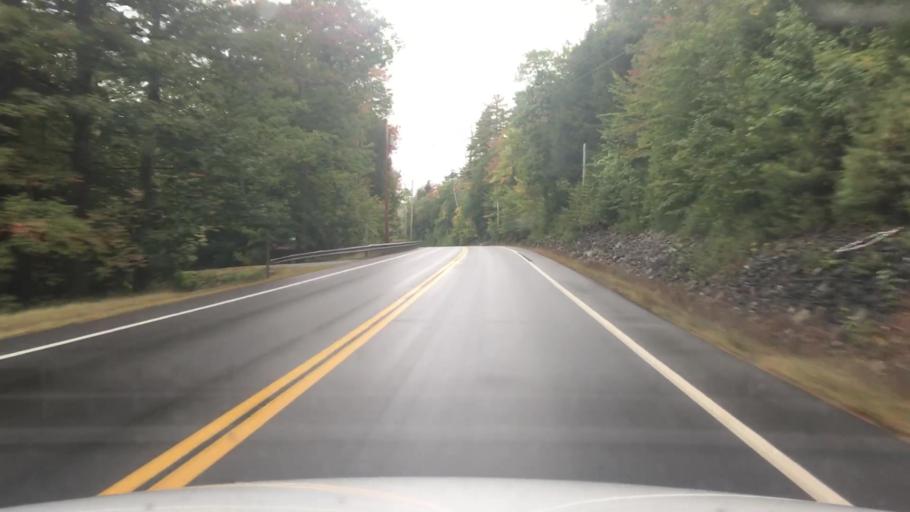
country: US
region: Maine
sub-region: Kennebec County
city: Rome
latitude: 44.5435
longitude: -69.8923
